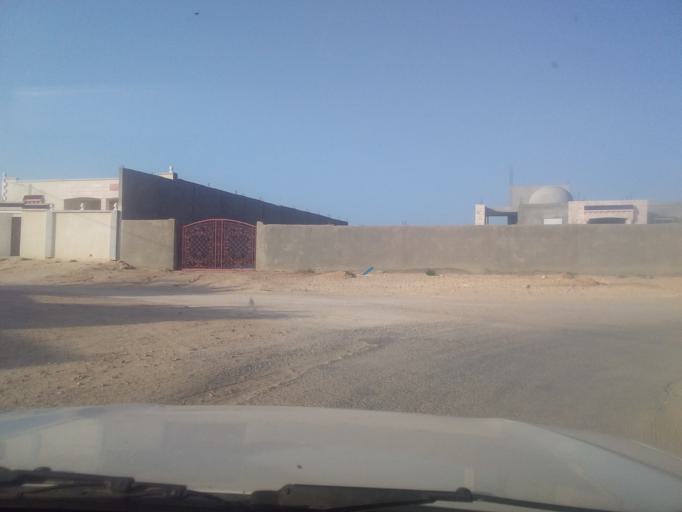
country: TN
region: Qabis
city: Gabes
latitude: 33.6366
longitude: 10.2881
